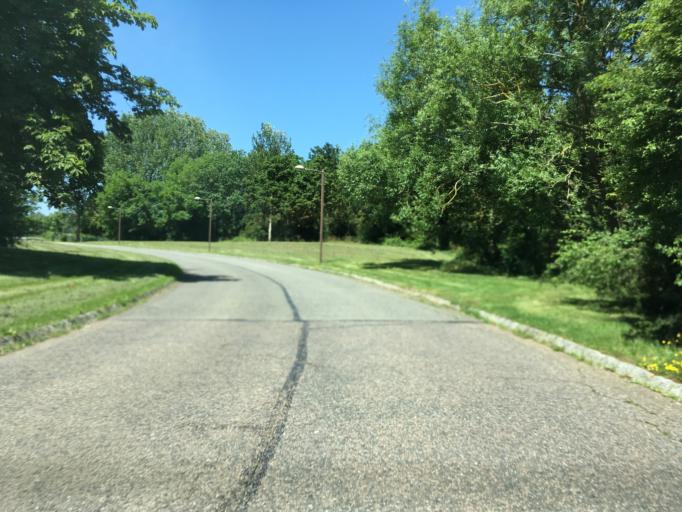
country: GB
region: England
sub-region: Milton Keynes
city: Simpson
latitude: 52.0351
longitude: -0.7236
